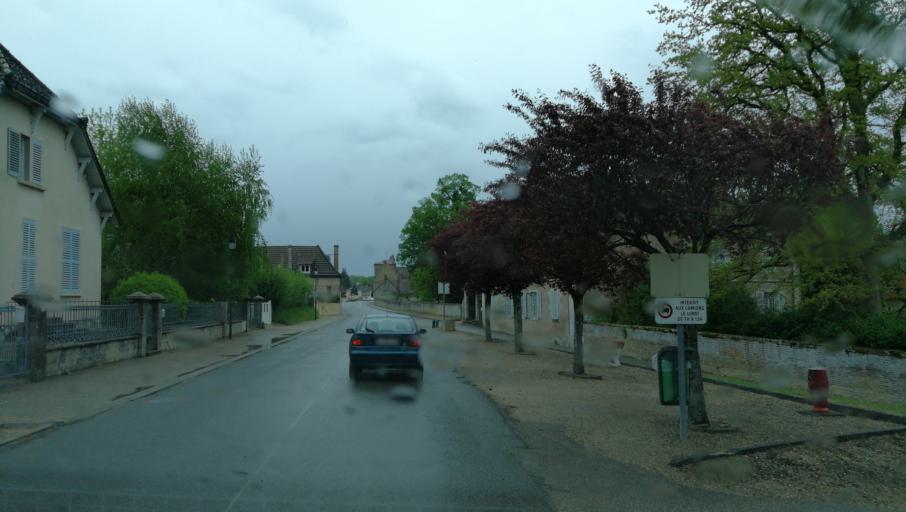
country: FR
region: Bourgogne
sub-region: Departement de Saone-et-Loire
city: Pierre-de-Bresse
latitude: 46.8867
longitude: 5.2582
